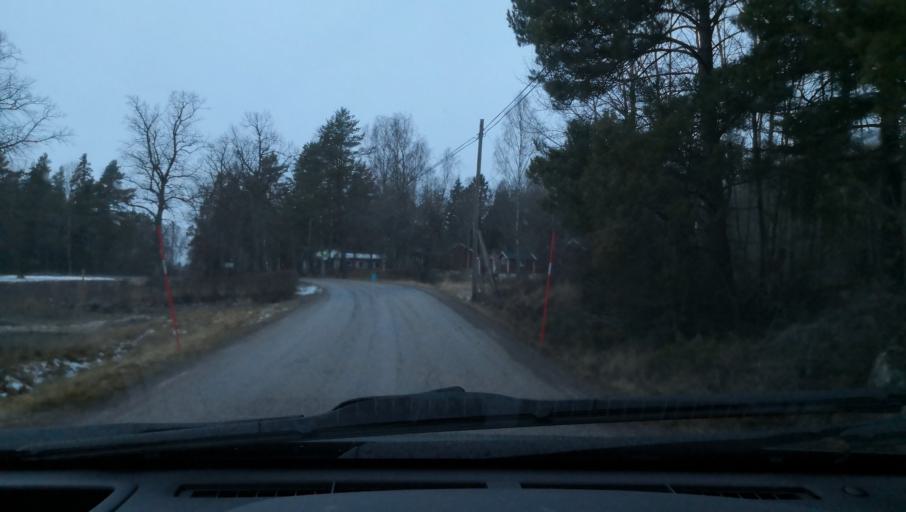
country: SE
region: Uppsala
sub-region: Enkopings Kommun
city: Hummelsta
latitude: 59.4563
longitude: 16.8531
